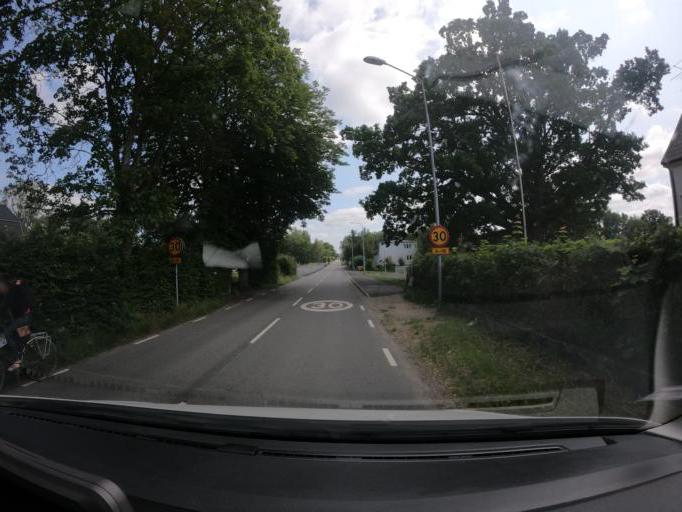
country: SE
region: Skane
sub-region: Hassleholms Kommun
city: Sosdala
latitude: 56.0412
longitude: 13.6718
